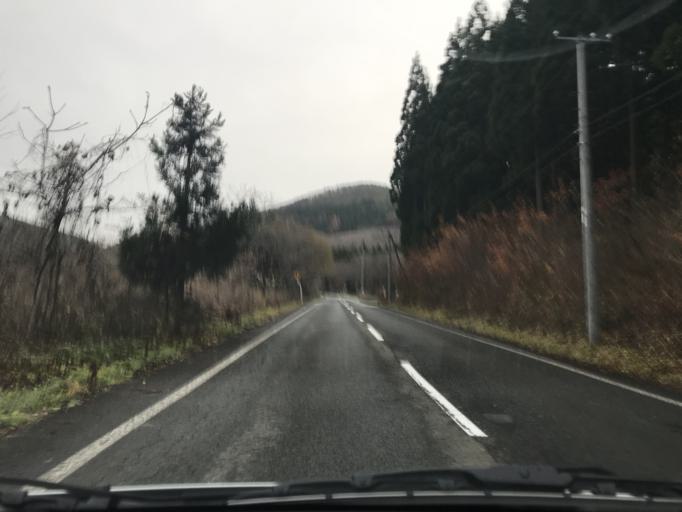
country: JP
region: Iwate
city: Tono
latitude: 39.1777
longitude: 141.3634
